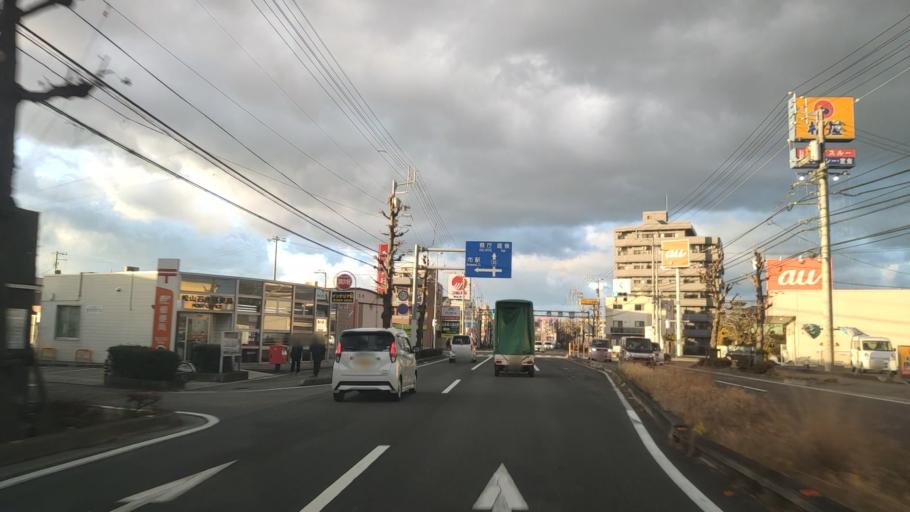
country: JP
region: Ehime
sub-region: Shikoku-chuo Shi
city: Matsuyama
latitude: 33.8111
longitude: 132.7793
